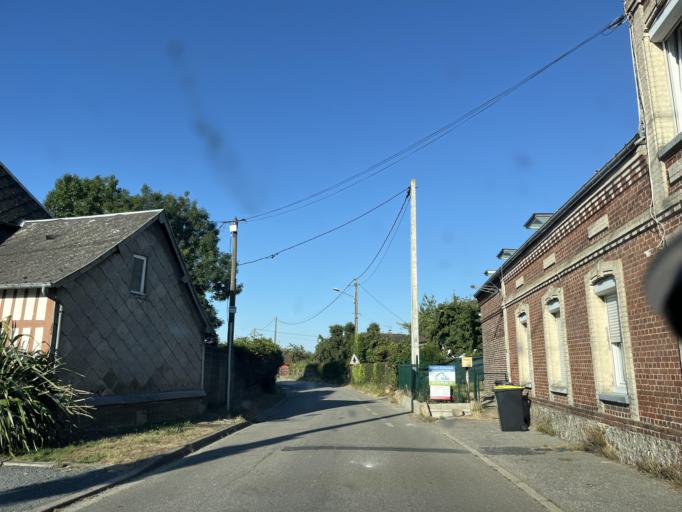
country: FR
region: Haute-Normandie
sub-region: Departement de la Seine-Maritime
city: Lanquetot
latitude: 49.5729
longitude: 0.5999
